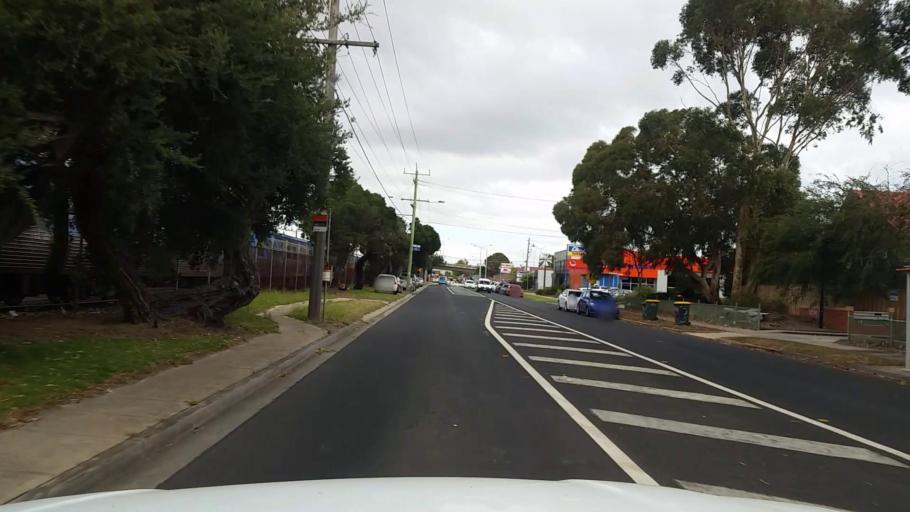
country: AU
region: Victoria
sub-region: Frankston
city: Frankston East
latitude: -38.1374
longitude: 145.1283
